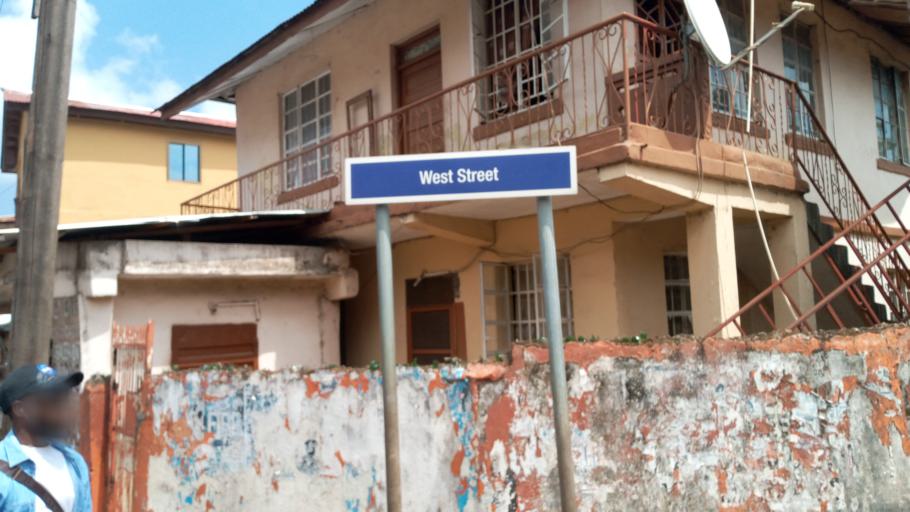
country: SL
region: Western Area
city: Freetown
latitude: 8.4779
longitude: -13.2380
